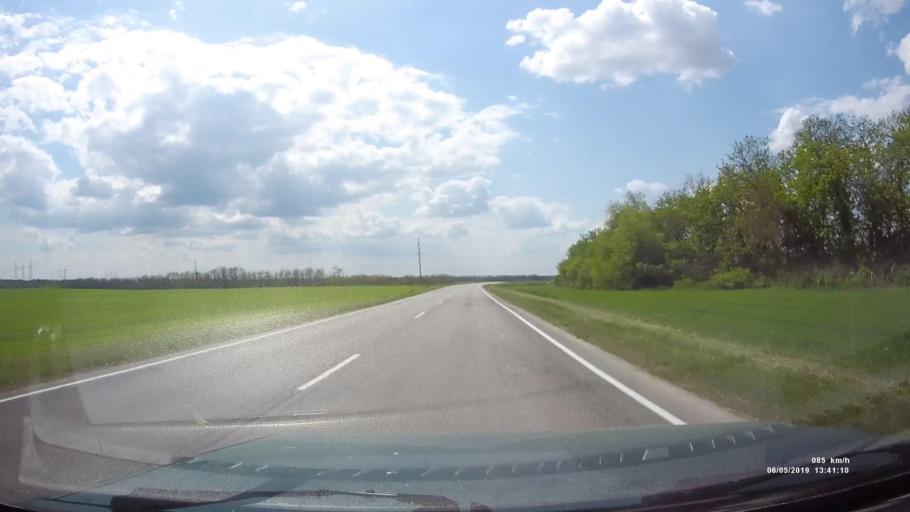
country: RU
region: Rostov
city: Ust'-Donetskiy
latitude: 47.6637
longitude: 40.6818
